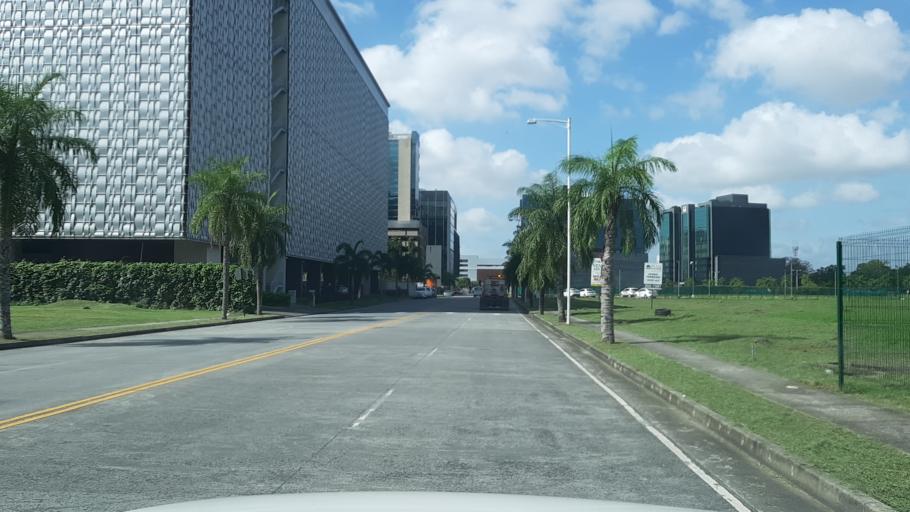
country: PA
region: Panama
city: San Miguelito
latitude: 9.0293
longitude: -79.4594
